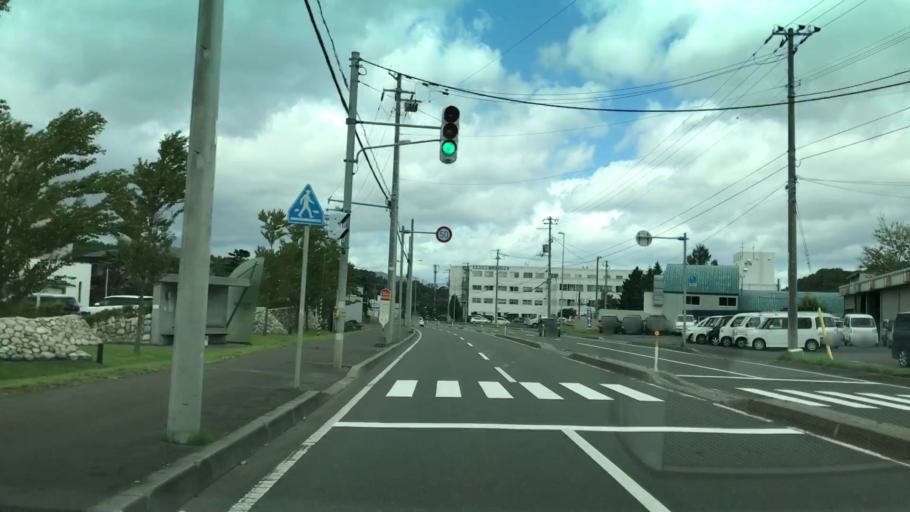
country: JP
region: Hokkaido
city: Kitahiroshima
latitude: 42.9772
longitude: 141.4457
